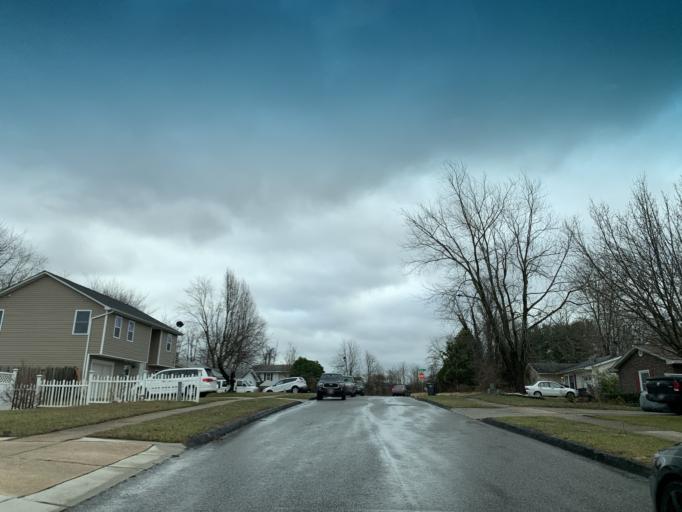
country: US
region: Maryland
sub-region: Harford County
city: Edgewood
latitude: 39.4303
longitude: -76.3130
